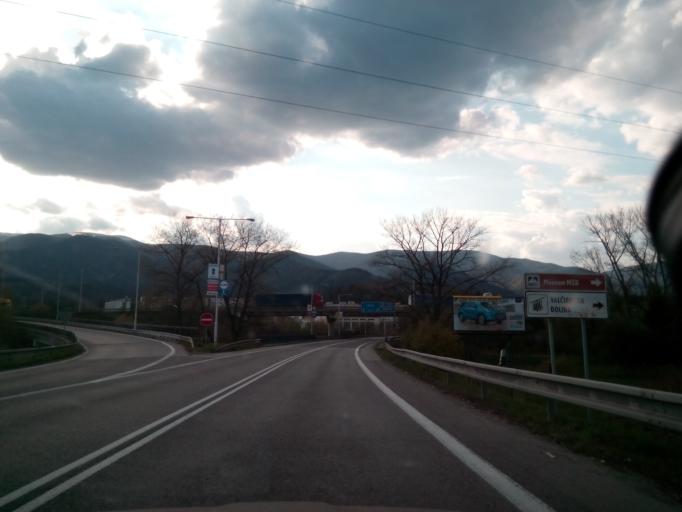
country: SK
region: Zilinsky
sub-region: Okres Zilina
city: Vrutky
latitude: 49.0934
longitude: 18.9267
